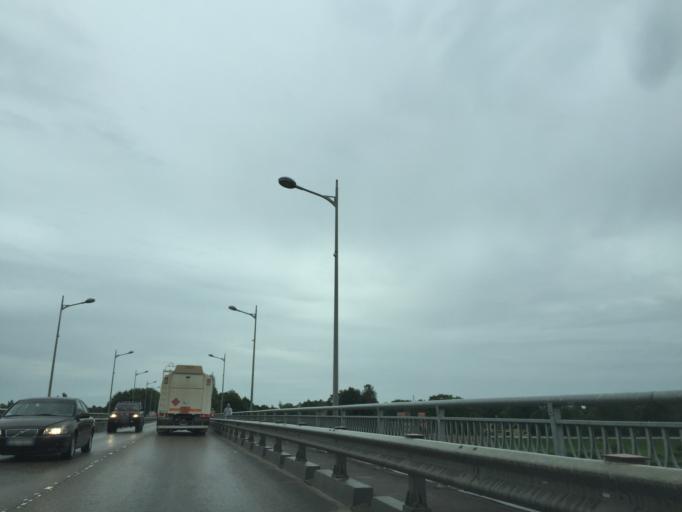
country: LV
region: Jekabpils Rajons
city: Jekabpils
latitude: 56.5007
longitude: 25.8785
